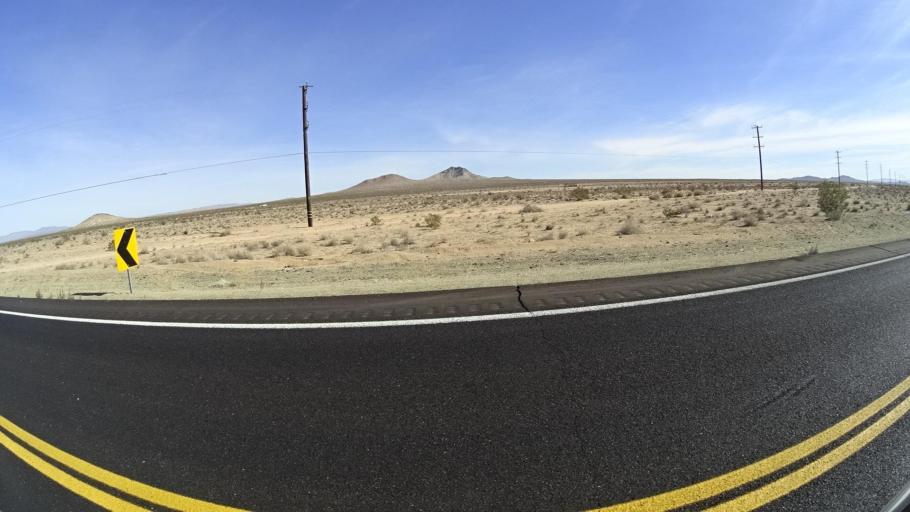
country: US
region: California
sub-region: Kern County
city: California City
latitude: 35.1017
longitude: -117.9178
